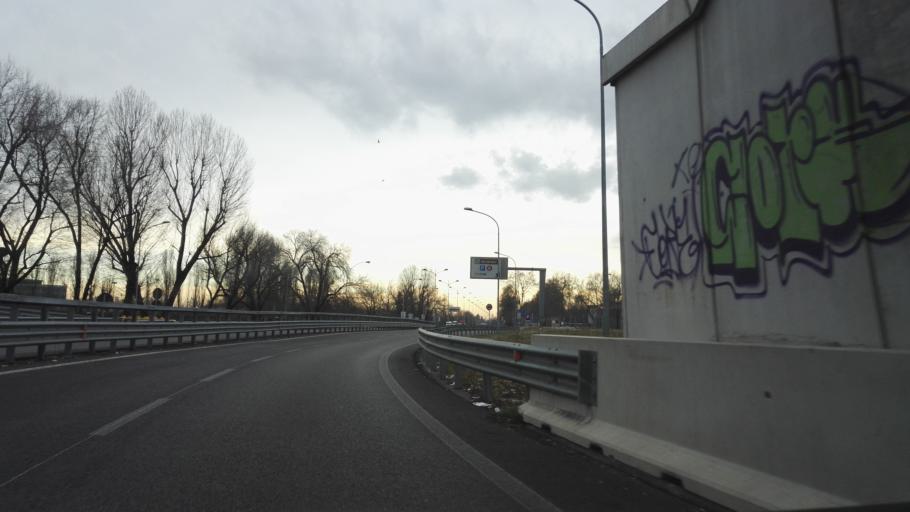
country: IT
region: Lombardy
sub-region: Citta metropolitana di Milano
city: Novegro-Tregarezzo-San Felice
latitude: 45.4757
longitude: 9.2957
